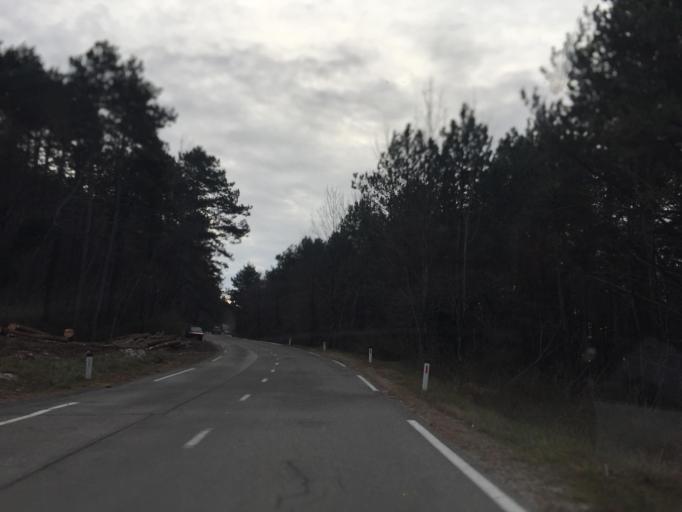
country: SI
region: Nova Gorica
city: Sempas
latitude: 45.9762
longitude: 13.7177
